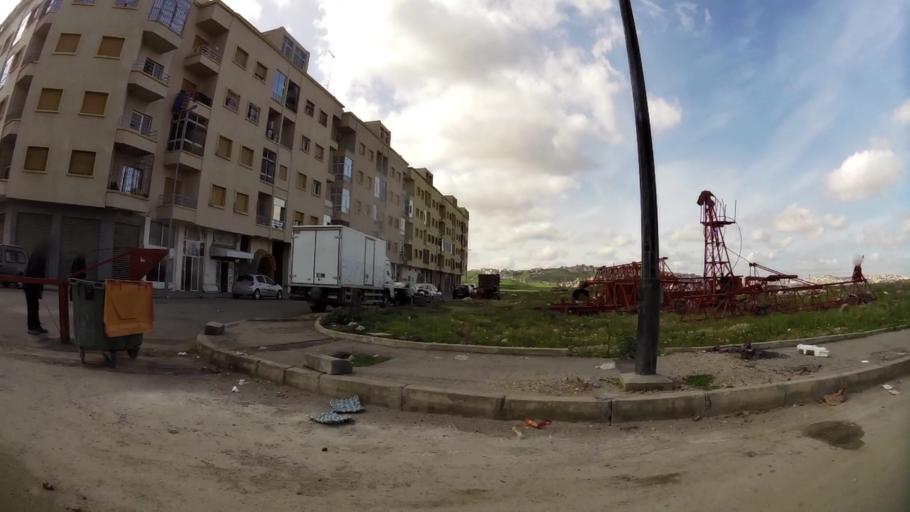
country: MA
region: Tanger-Tetouan
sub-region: Tanger-Assilah
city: Tangier
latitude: 35.7639
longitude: -5.7700
